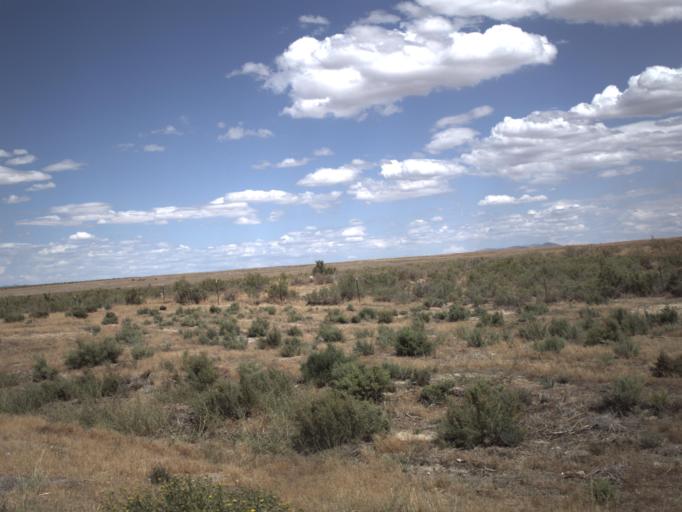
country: US
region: Utah
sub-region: Millard County
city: Delta
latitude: 39.3270
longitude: -112.4852
